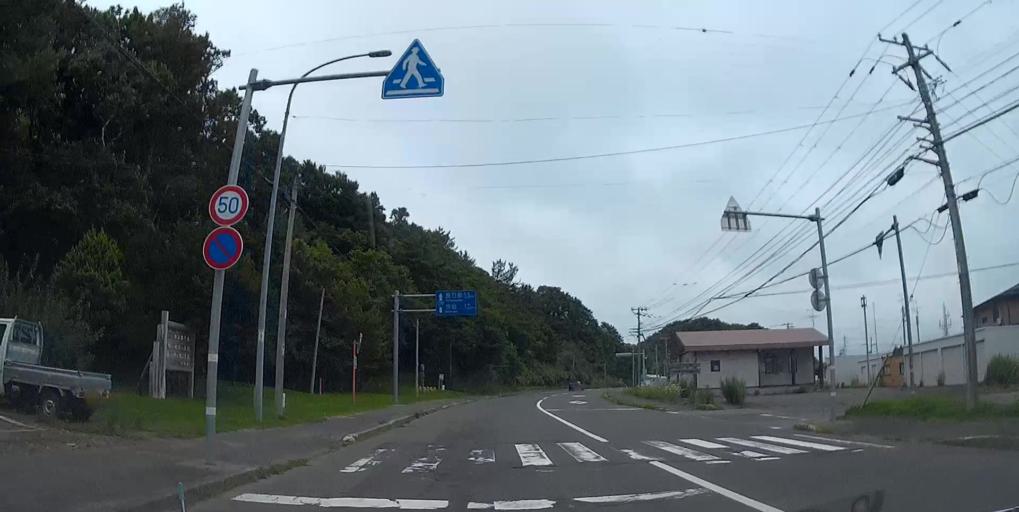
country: JP
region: Hokkaido
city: Iwanai
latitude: 42.4138
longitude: 139.8822
